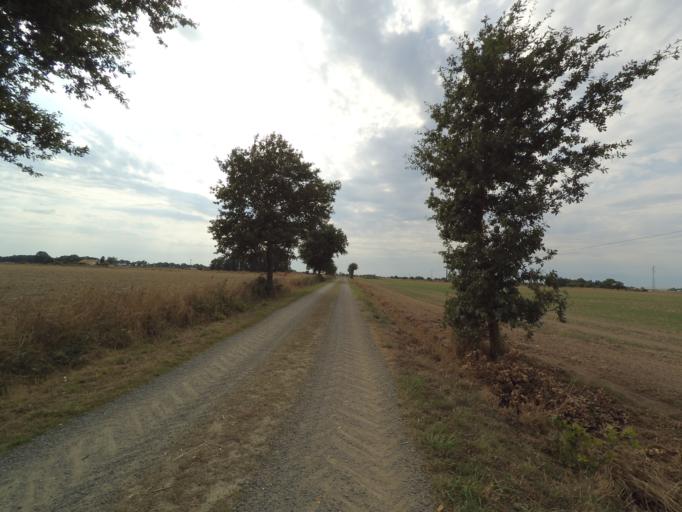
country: FR
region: Pays de la Loire
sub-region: Departement de la Vendee
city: Bouffere
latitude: 46.9763
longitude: -1.3843
